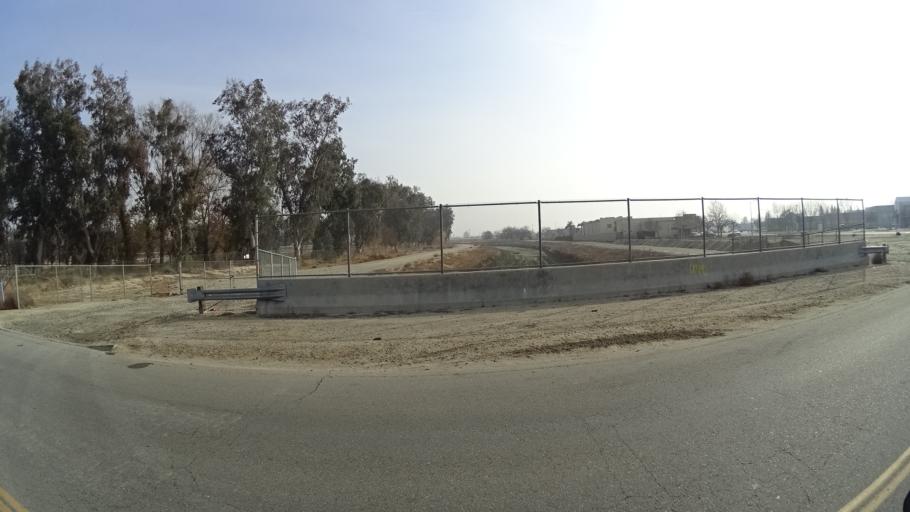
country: US
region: California
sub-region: Kern County
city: Oildale
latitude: 35.3966
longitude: -119.0390
